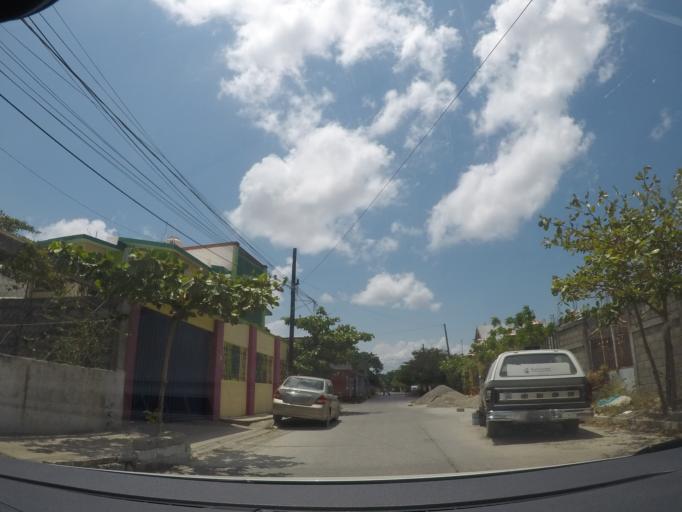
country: MX
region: Oaxaca
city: Juchitan de Zaragoza
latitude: 16.4416
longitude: -95.0112
